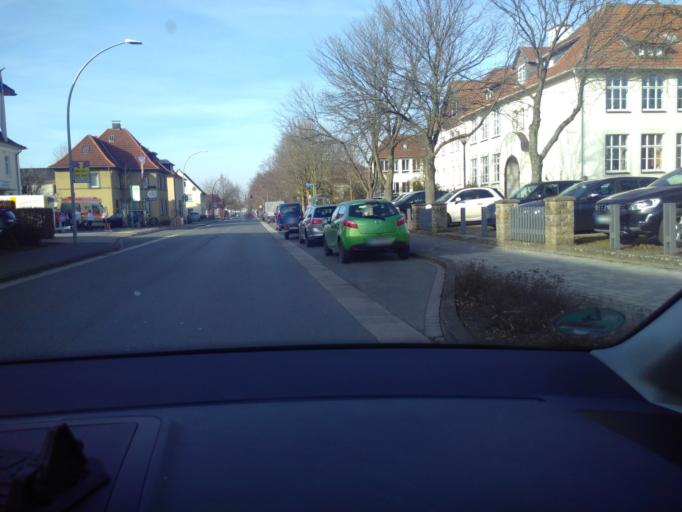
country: DE
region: North Rhine-Westphalia
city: Rietberg
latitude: 51.8316
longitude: 8.4424
